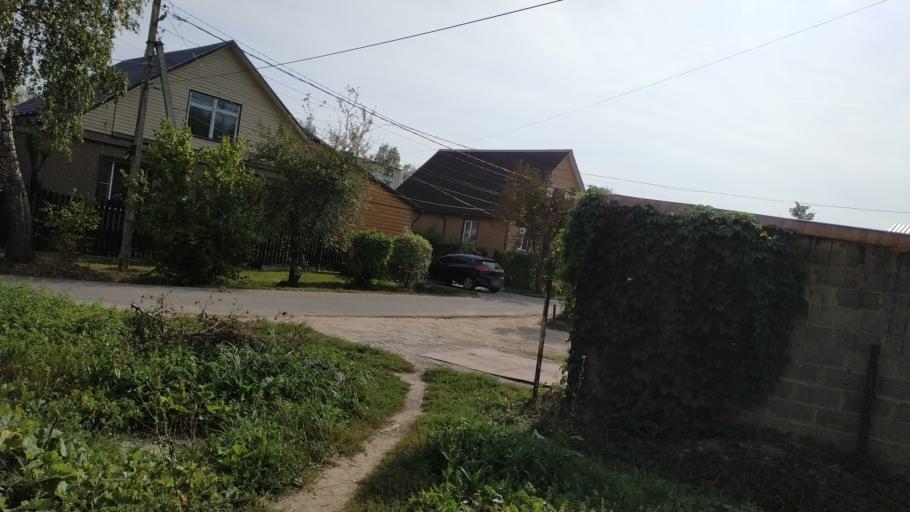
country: RU
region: Moskovskaya
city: Bronnitsy
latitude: 55.4220
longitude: 38.2886
